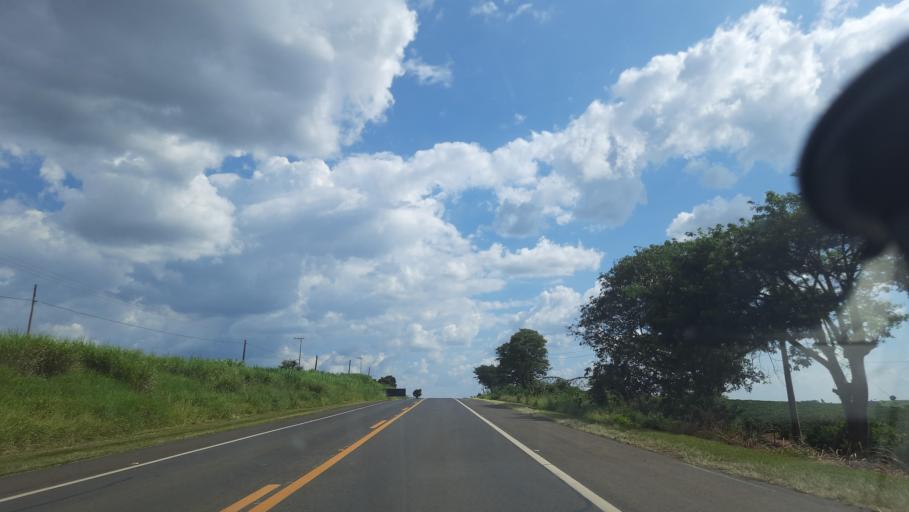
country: BR
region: Sao Paulo
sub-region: Sao Jose Do Rio Pardo
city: Sao Jose do Rio Pardo
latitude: -21.6735
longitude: -46.9236
